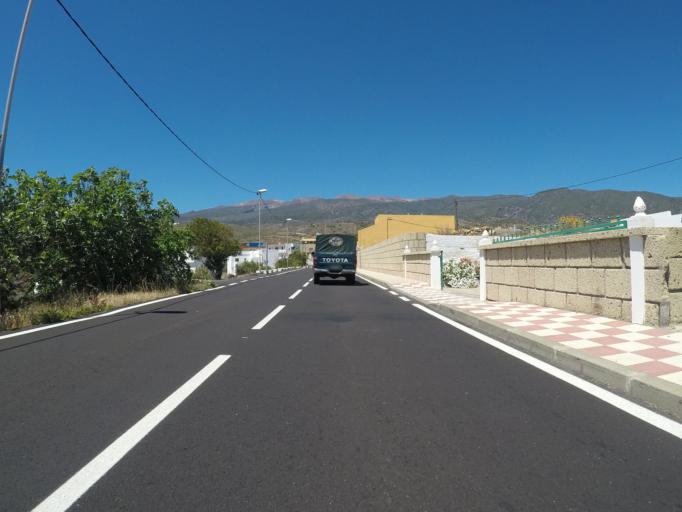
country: ES
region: Canary Islands
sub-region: Provincia de Santa Cruz de Tenerife
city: Lomo de Arico
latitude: 28.1708
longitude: -16.4953
